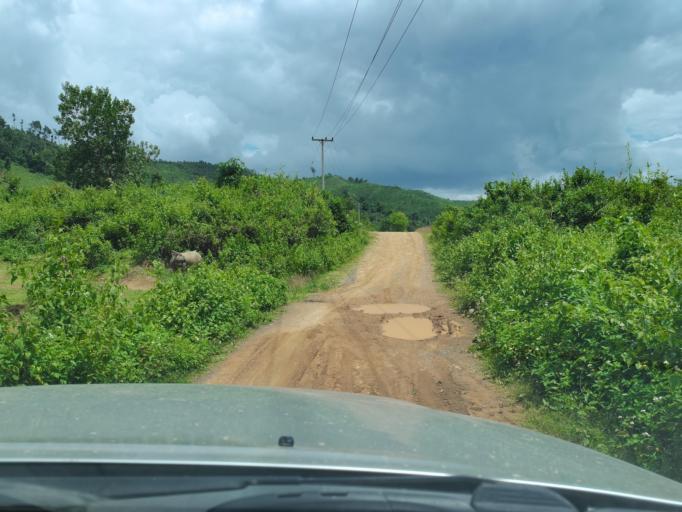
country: LA
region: Loungnamtha
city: Muang Long
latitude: 20.7261
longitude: 101.0141
